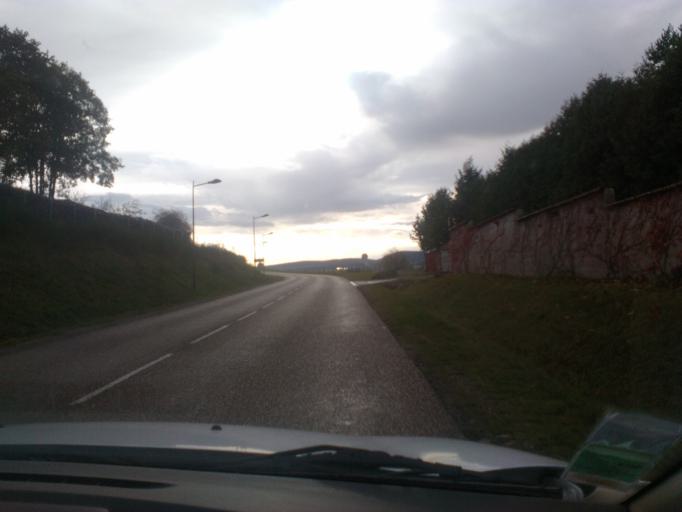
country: FR
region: Lorraine
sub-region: Departement des Vosges
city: Corcieux
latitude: 48.1755
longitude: 6.8331
